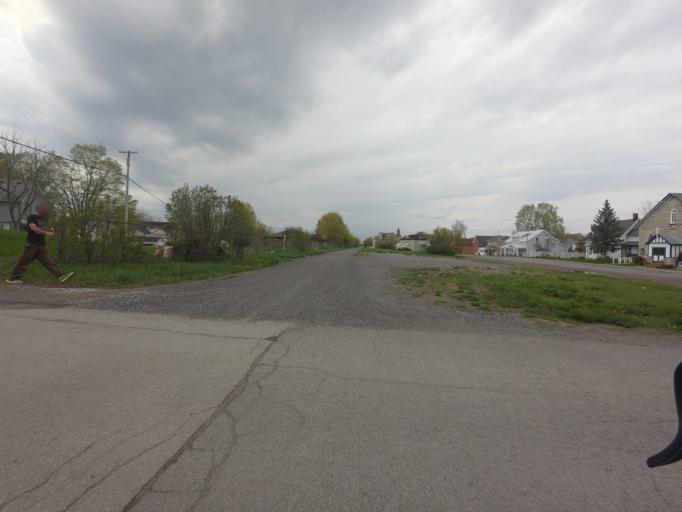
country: CA
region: Ontario
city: Carleton Place
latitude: 45.2238
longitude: -76.1916
